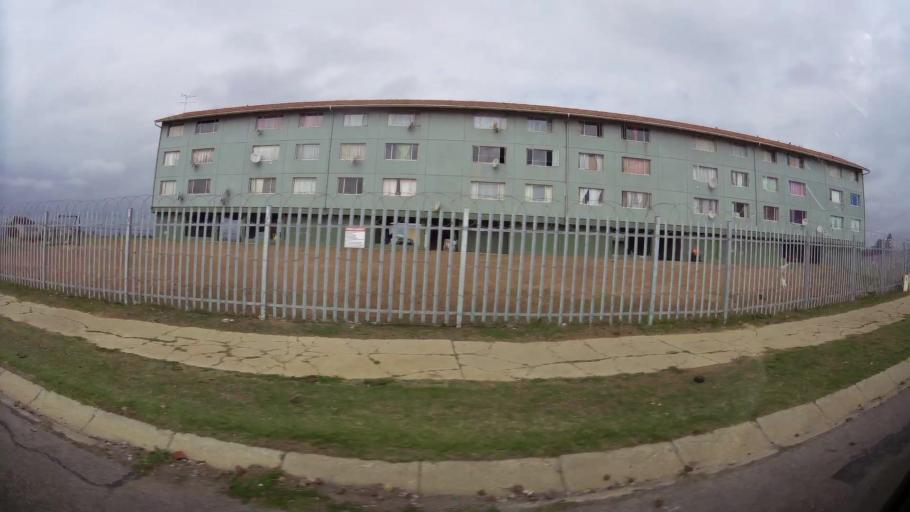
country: ZA
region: Eastern Cape
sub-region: Nelson Mandela Bay Metropolitan Municipality
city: Port Elizabeth
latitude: -33.8944
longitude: 25.5538
